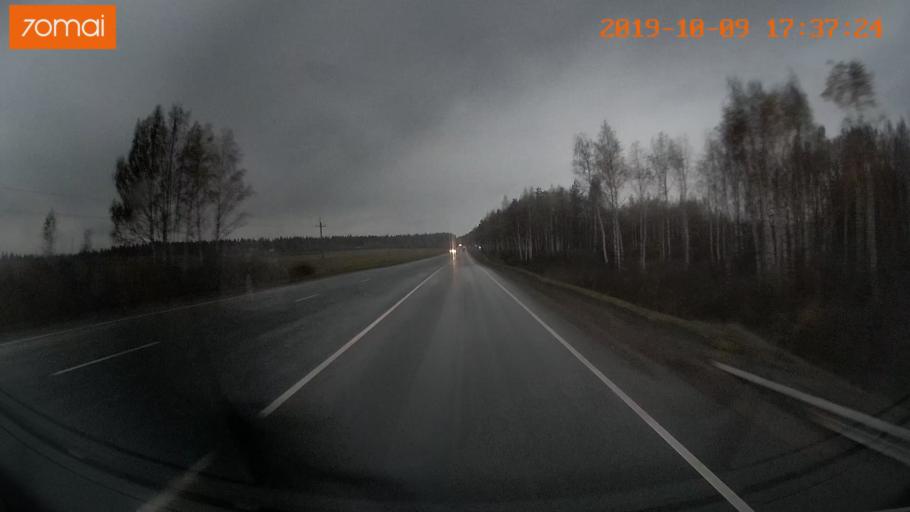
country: RU
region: Ivanovo
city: Bogorodskoye
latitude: 57.0709
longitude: 40.9801
